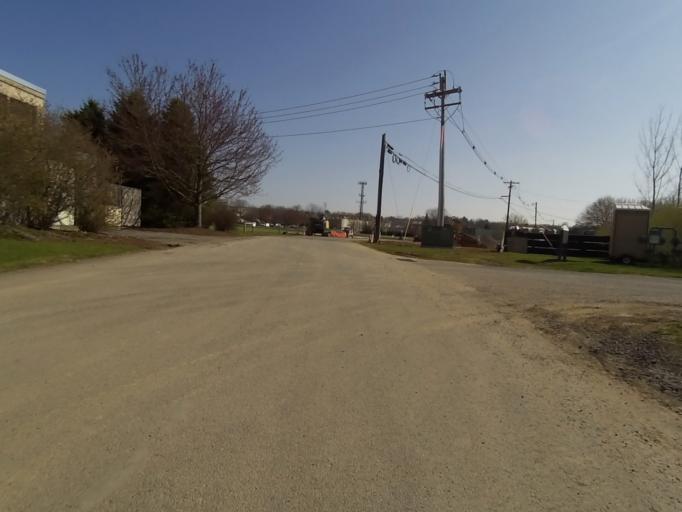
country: US
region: Pennsylvania
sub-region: Centre County
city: State College
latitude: 40.8140
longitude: -77.8692
